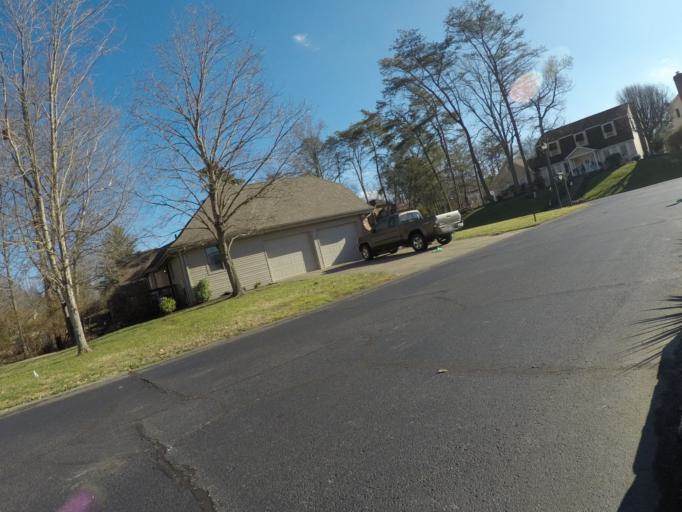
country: US
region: West Virginia
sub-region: Cabell County
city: Pea Ridge
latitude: 38.4210
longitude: -82.3276
